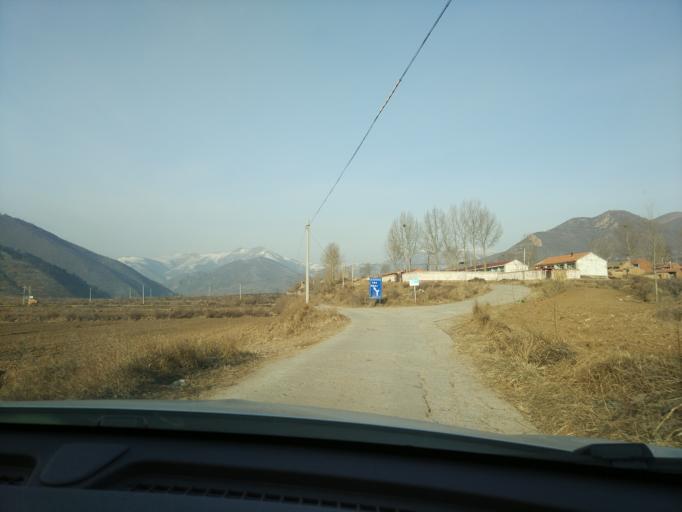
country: CN
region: Hebei
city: Xiwanzi
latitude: 40.8443
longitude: 115.5219
